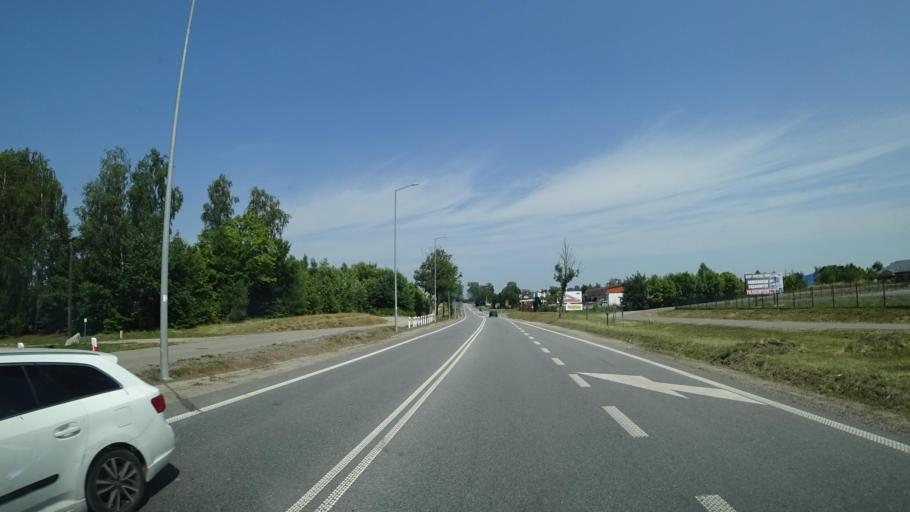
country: PL
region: Pomeranian Voivodeship
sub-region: Powiat koscierski
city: Koscierzyna
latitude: 54.1383
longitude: 18.0157
